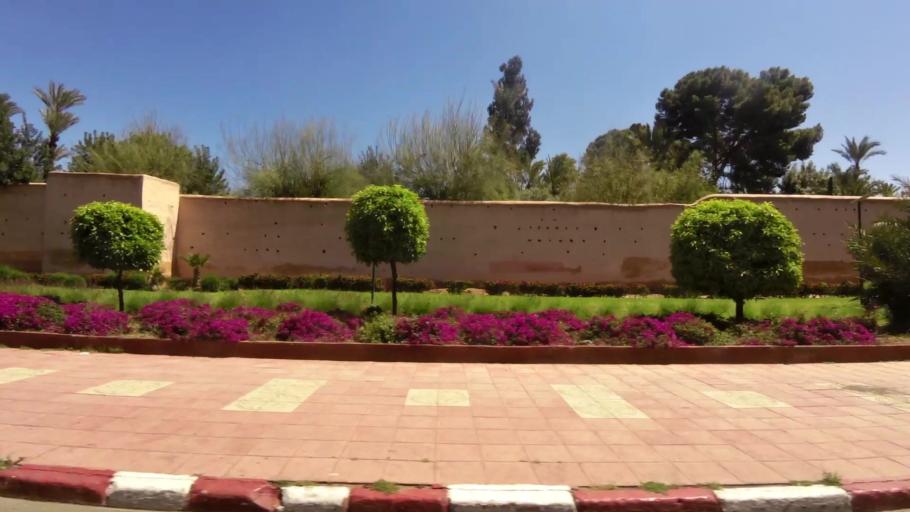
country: MA
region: Marrakech-Tensift-Al Haouz
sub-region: Marrakech
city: Marrakesh
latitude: 31.6264
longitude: -8.0015
